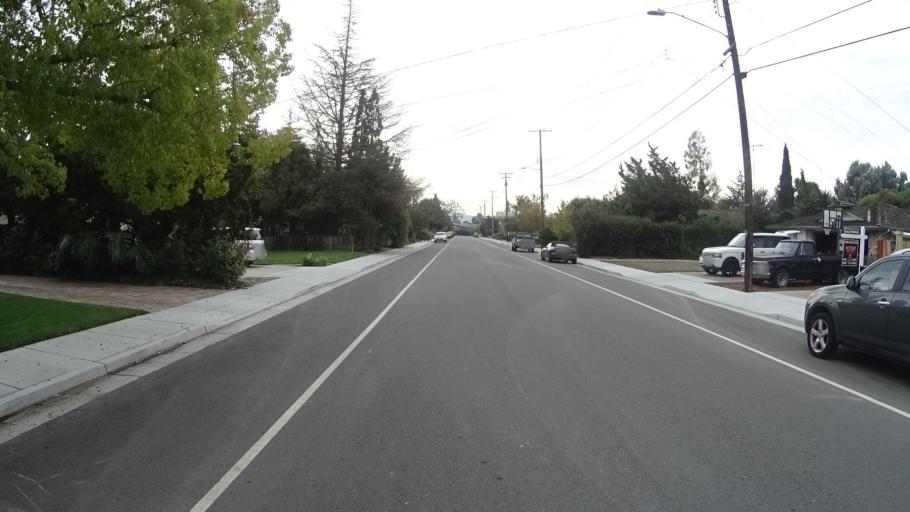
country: US
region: California
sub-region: Santa Clara County
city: Burbank
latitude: 37.3265
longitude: -121.9563
